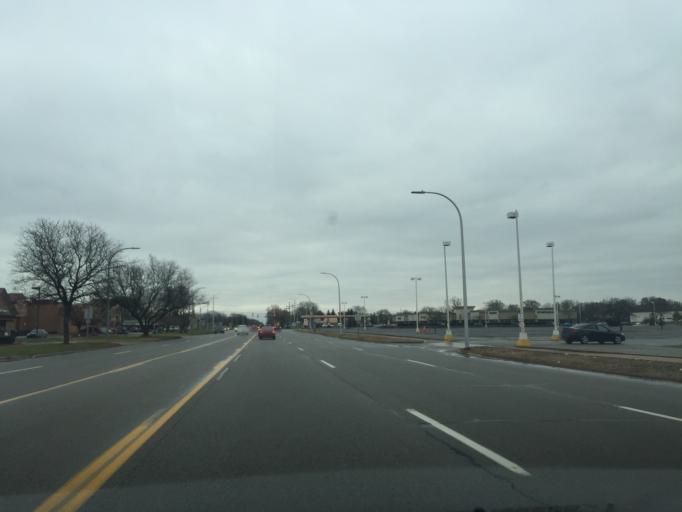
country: US
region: Michigan
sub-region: Oakland County
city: Farmington
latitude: 42.4292
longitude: -83.3360
